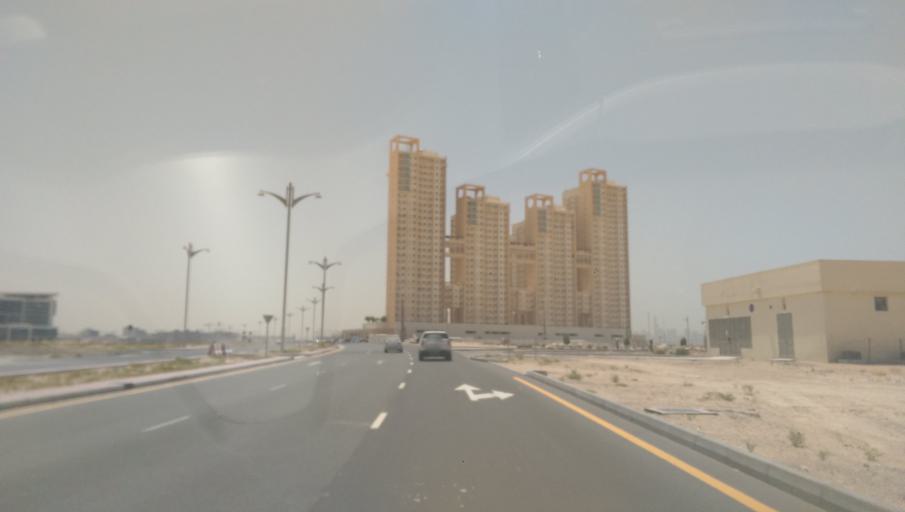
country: AE
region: Dubai
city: Dubai
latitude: 25.0388
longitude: 55.1972
